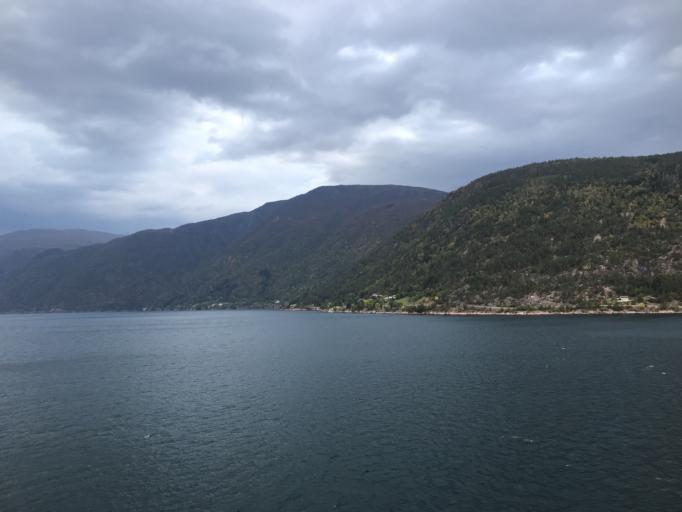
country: NO
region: Sogn og Fjordane
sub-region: Leikanger
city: Hermansverk
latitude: 61.1742
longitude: 6.7121
